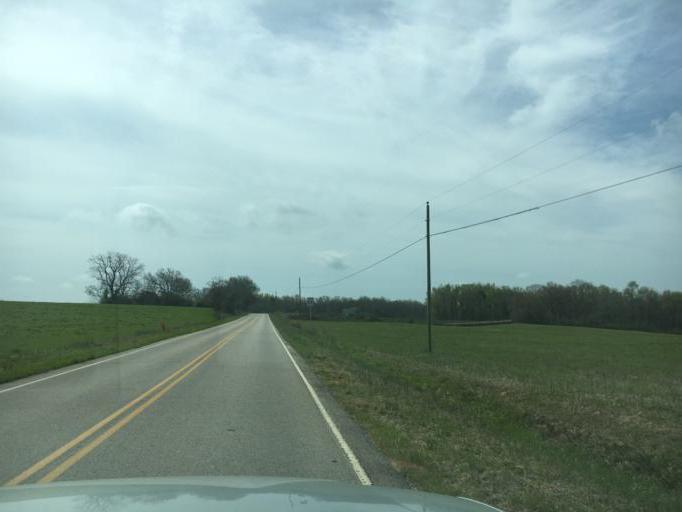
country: US
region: Georgia
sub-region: Hart County
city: Royston
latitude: 34.3352
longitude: -83.0389
